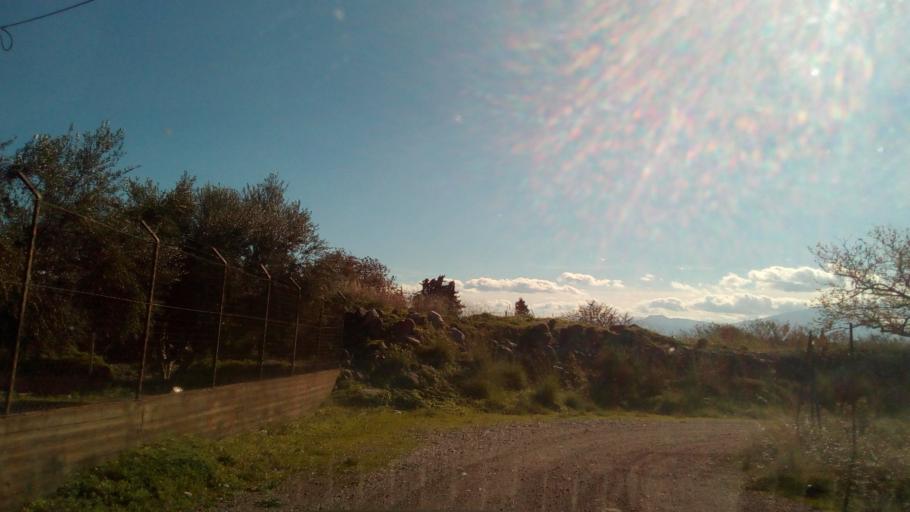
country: GR
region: West Greece
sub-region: Nomos Achaias
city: Kamarai
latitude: 38.3944
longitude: 22.0012
